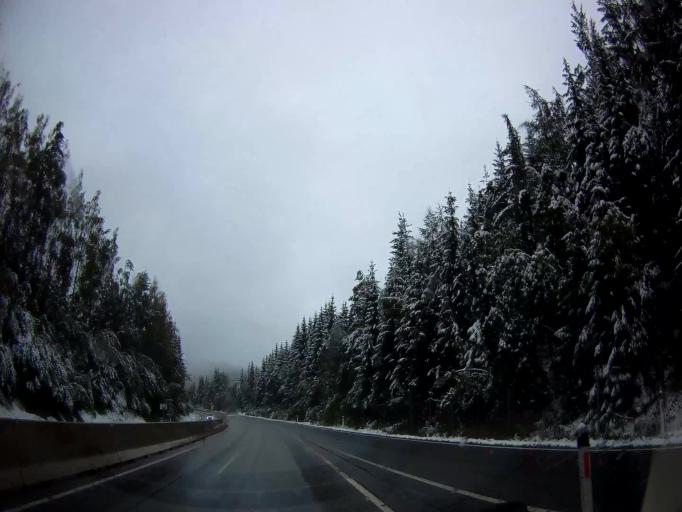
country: AT
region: Salzburg
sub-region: Politischer Bezirk Sankt Johann im Pongau
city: Bischofshofen
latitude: 47.4319
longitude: 13.2258
